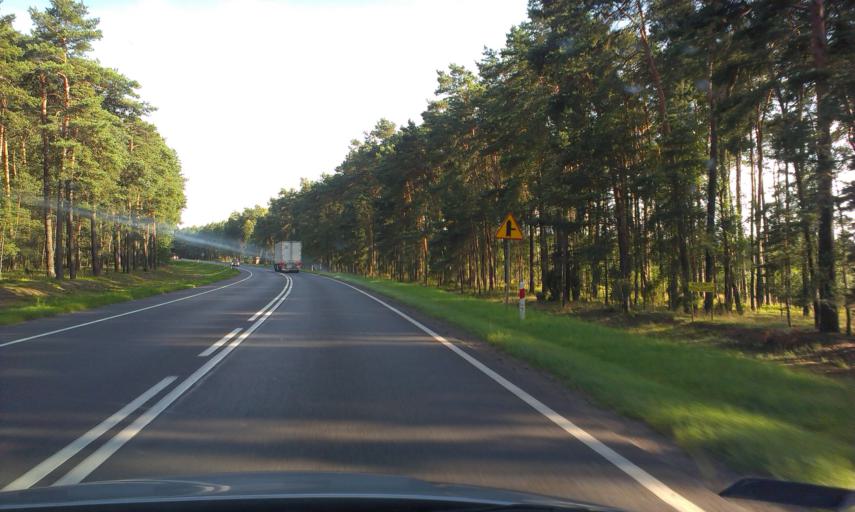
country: PL
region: Kujawsko-Pomorskie
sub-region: Powiat bydgoski
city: Biale Blota
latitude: 53.1083
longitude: 17.8847
